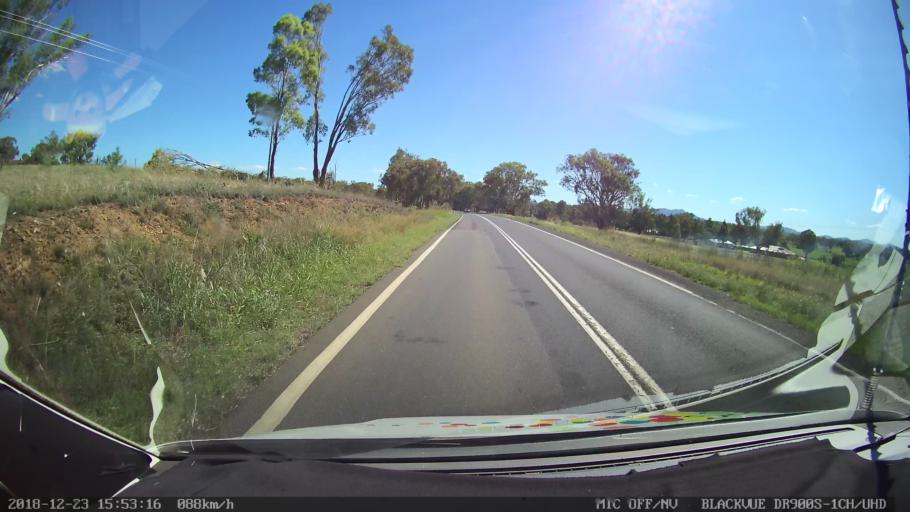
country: AU
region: New South Wales
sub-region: Tamworth Municipality
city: Phillip
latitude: -31.1315
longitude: 150.8822
